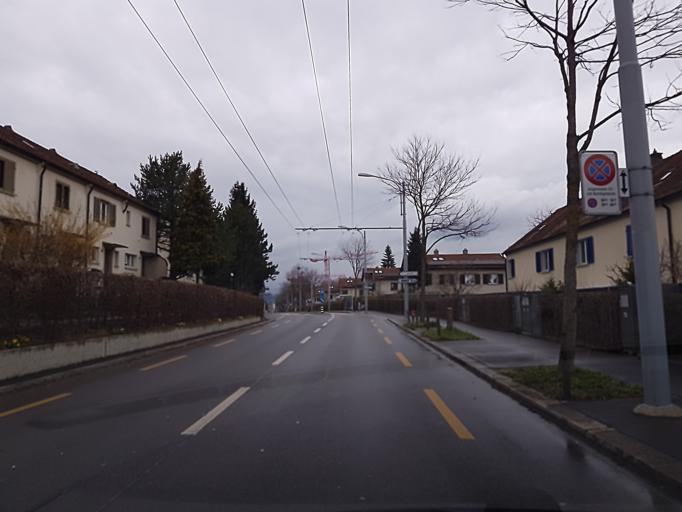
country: CH
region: Zurich
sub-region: Bezirk Zuerich
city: Zuerich (Kreis 3) / Alt-Wiedikon
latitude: 47.3559
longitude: 8.5104
